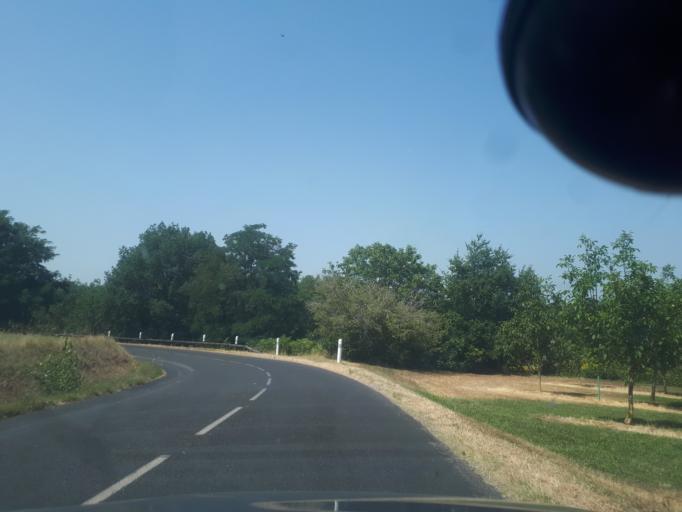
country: FR
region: Midi-Pyrenees
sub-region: Departement du Lot
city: Souillac
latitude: 44.8825
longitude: 1.4486
